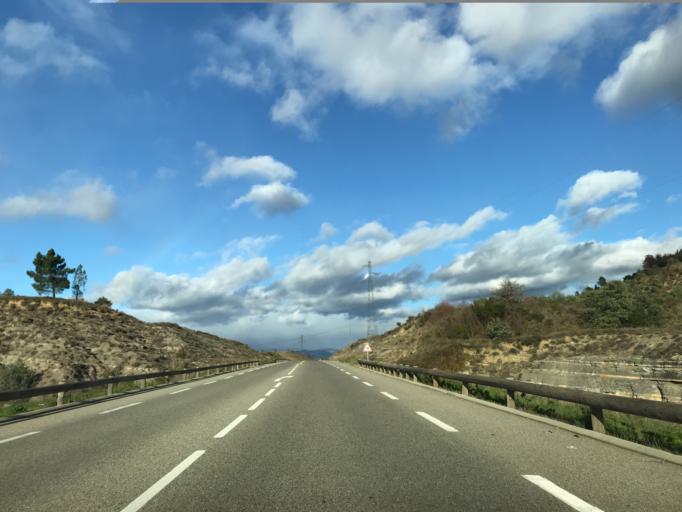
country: FR
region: Rhone-Alpes
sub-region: Departement de l'Ardeche
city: Lachapelle-sous-Aubenas
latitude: 44.5509
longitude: 4.3581
